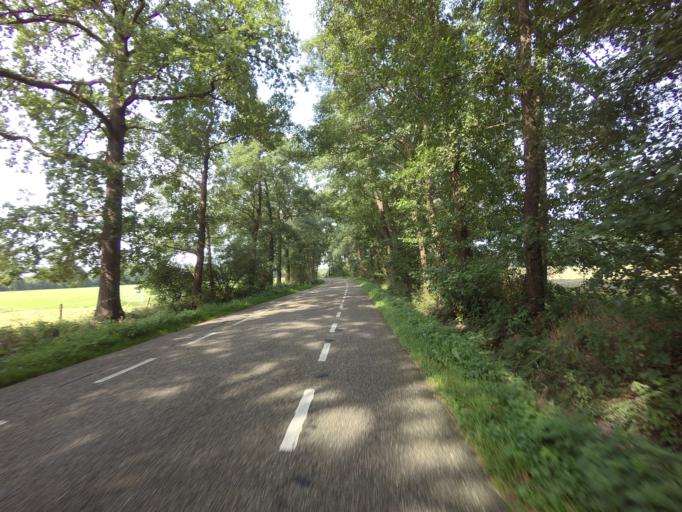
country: NL
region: Overijssel
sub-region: Gemeente Tubbergen
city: Tubbergen
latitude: 52.4276
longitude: 6.7774
